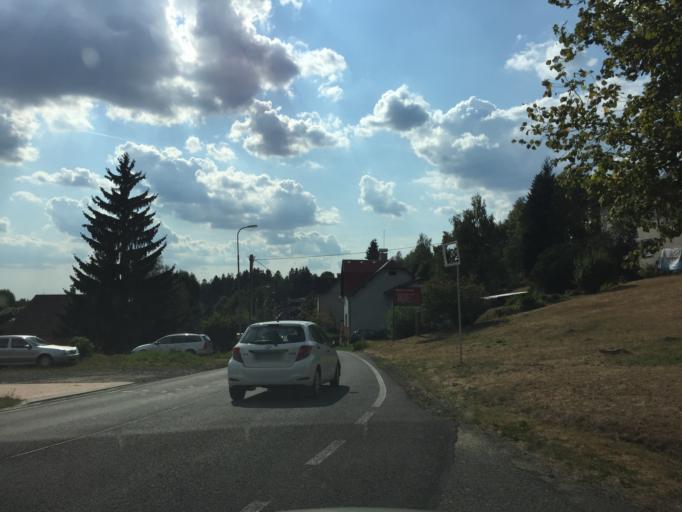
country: CZ
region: Liberecky
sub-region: Okres Jablonec nad Nisou
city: Jablonec nad Nisou
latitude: 50.7097
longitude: 15.1915
